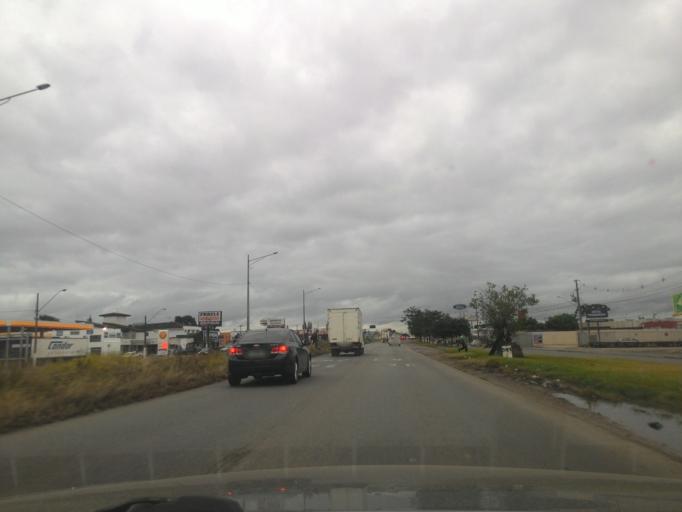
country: BR
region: Parana
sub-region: Sao Jose Dos Pinhais
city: Sao Jose dos Pinhais
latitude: -25.5301
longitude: -49.2992
